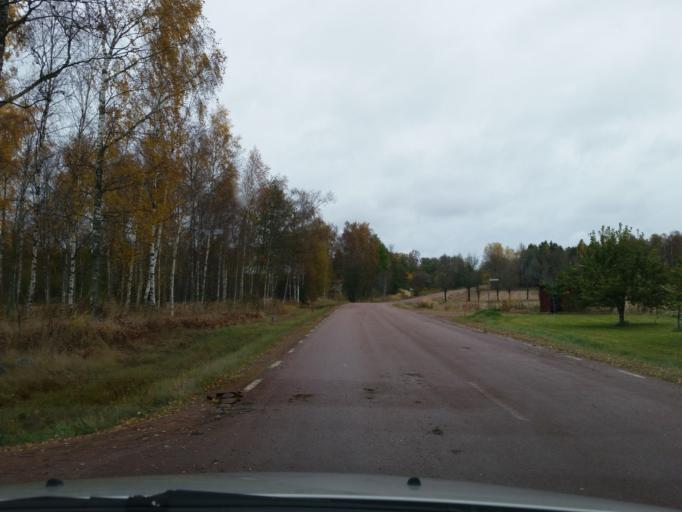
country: AX
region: Alands landsbygd
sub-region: Lemland
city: Lemland
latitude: 60.0623
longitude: 20.0979
